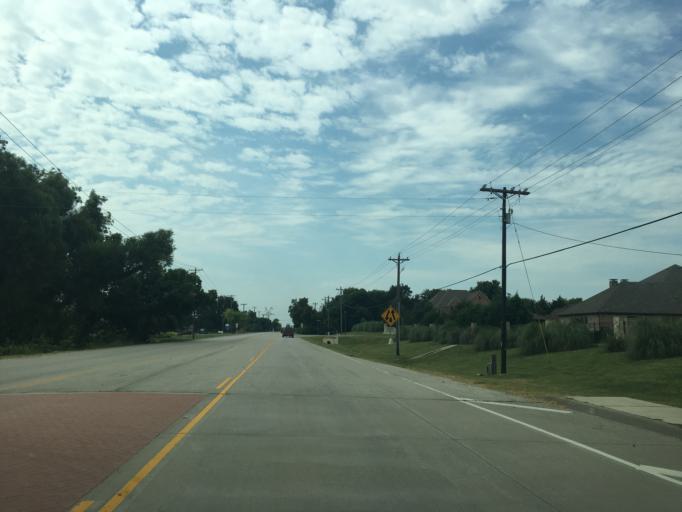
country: US
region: Texas
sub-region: Collin County
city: Wylie
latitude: 33.0013
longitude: -96.5220
